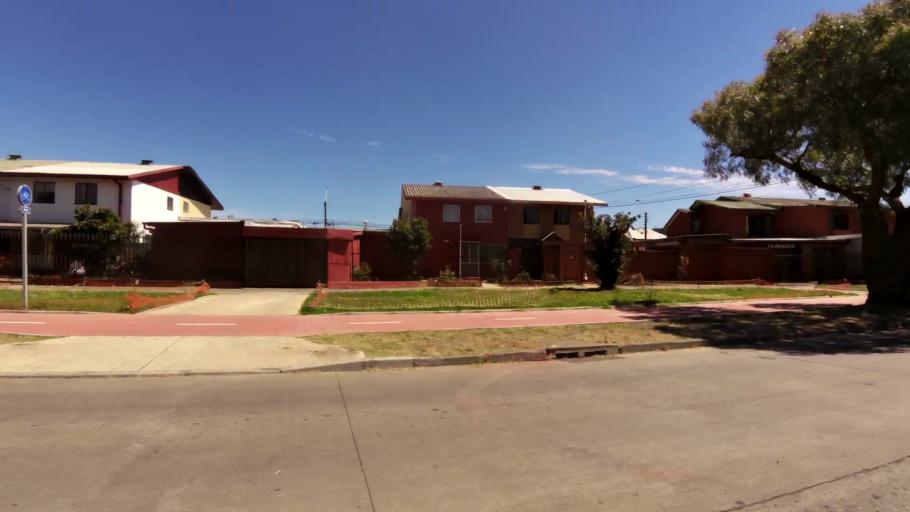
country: CL
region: Biobio
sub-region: Provincia de Concepcion
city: Talcahuano
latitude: -36.7607
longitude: -73.0937
